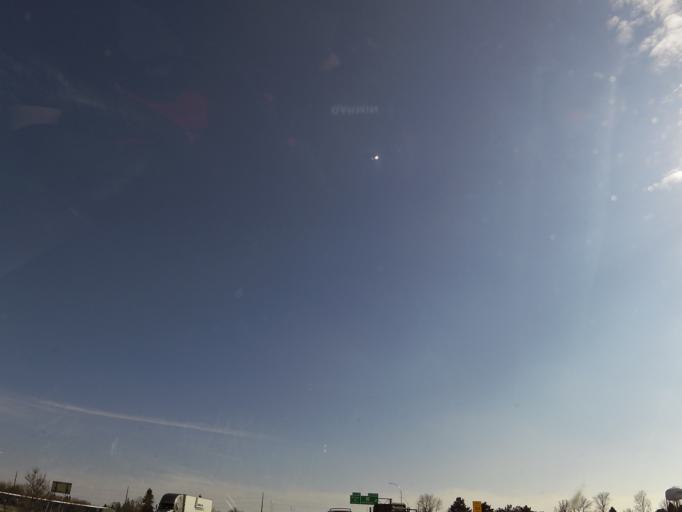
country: US
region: Minnesota
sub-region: Steele County
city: Owatonna
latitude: 44.0960
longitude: -93.2451
